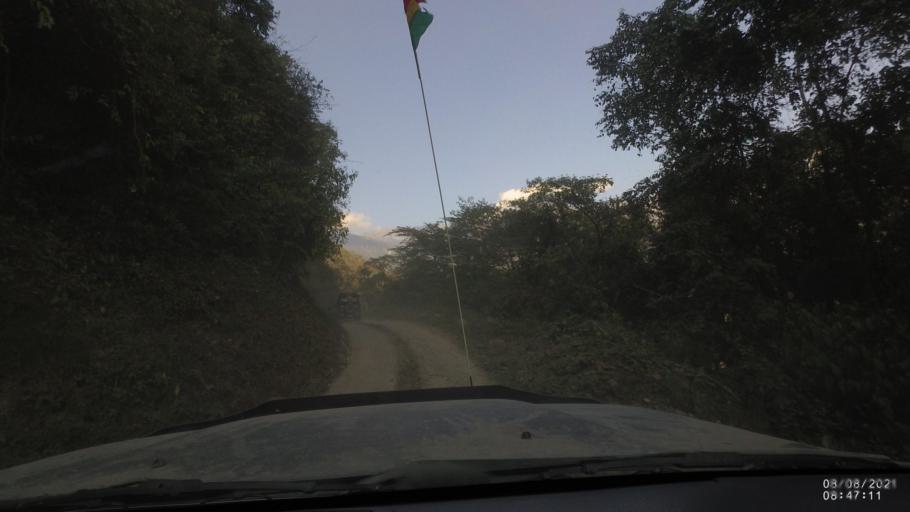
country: BO
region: La Paz
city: Quime
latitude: -16.5278
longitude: -66.7536
